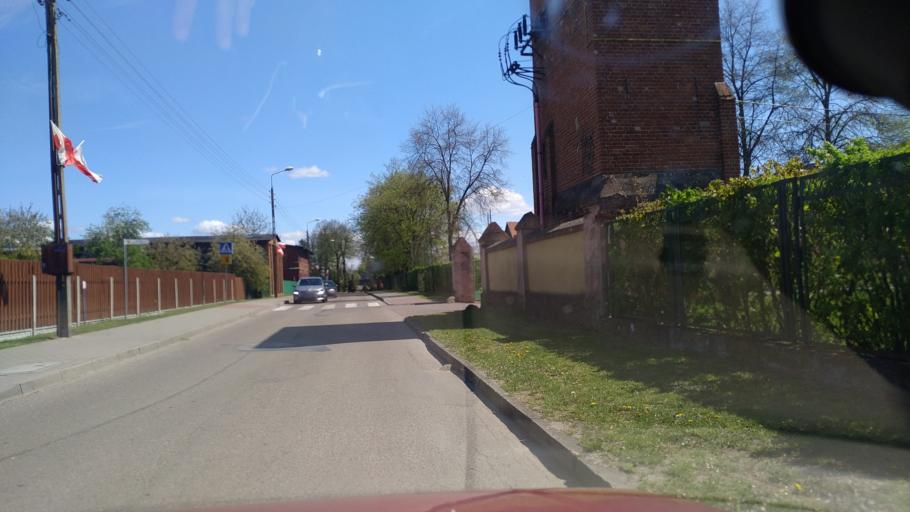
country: PL
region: Greater Poland Voivodeship
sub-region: Powiat zlotowski
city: Krajenka
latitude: 53.2980
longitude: 16.9851
